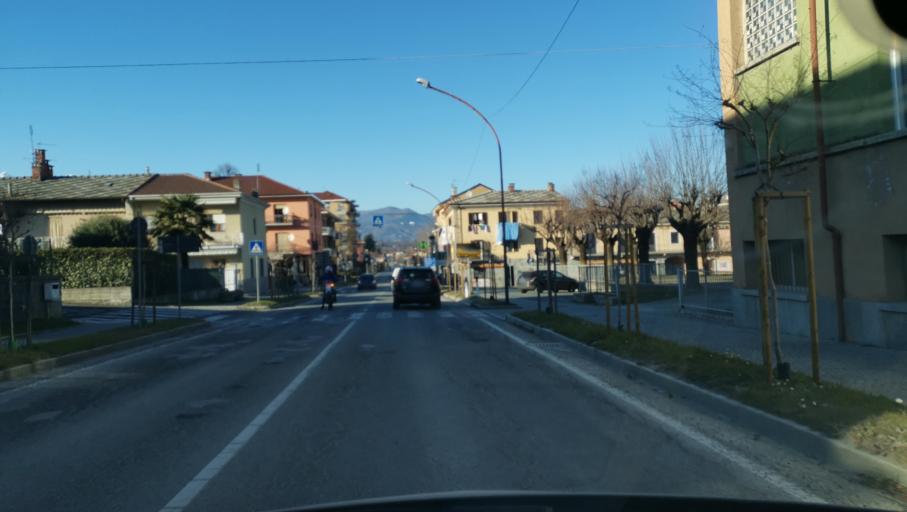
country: IT
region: Piedmont
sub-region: Provincia di Cuneo
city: Bagnolo Piemonte
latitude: 44.7611
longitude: 7.3154
